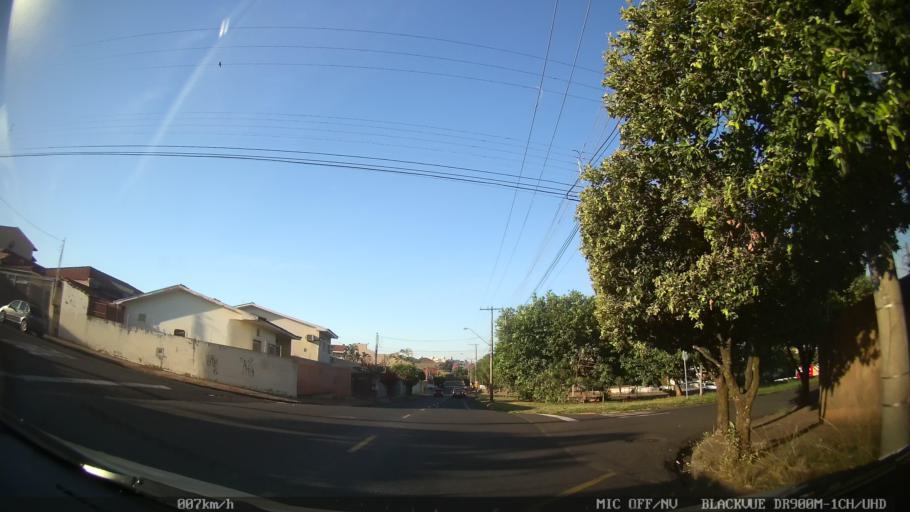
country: BR
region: Sao Paulo
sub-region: Sao Jose Do Rio Preto
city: Sao Jose do Rio Preto
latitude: -20.7967
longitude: -49.3604
